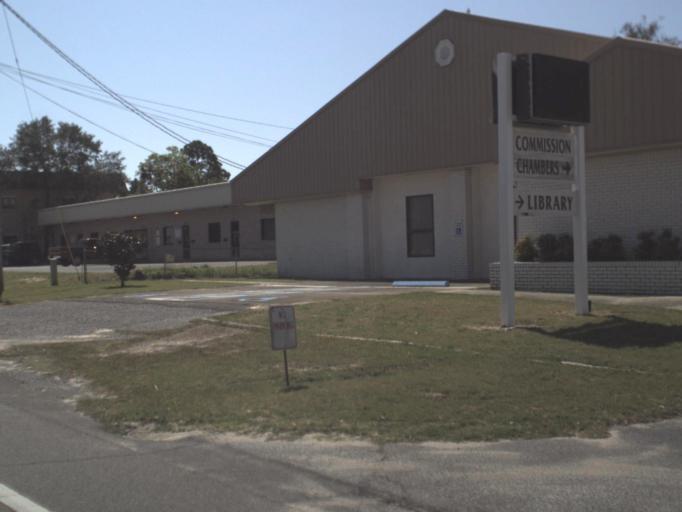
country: US
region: Florida
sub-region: Okaloosa County
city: Valparaiso
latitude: 30.5099
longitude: -86.4997
